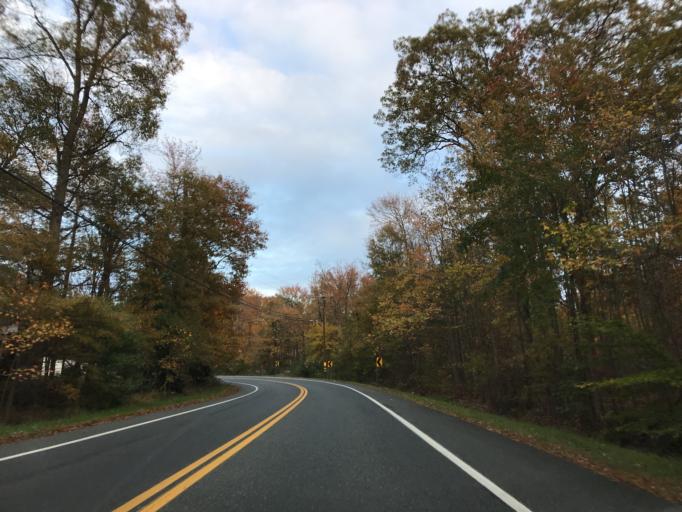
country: US
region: Maryland
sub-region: Baltimore County
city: Bowleys Quarters
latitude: 39.3652
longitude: -76.3678
